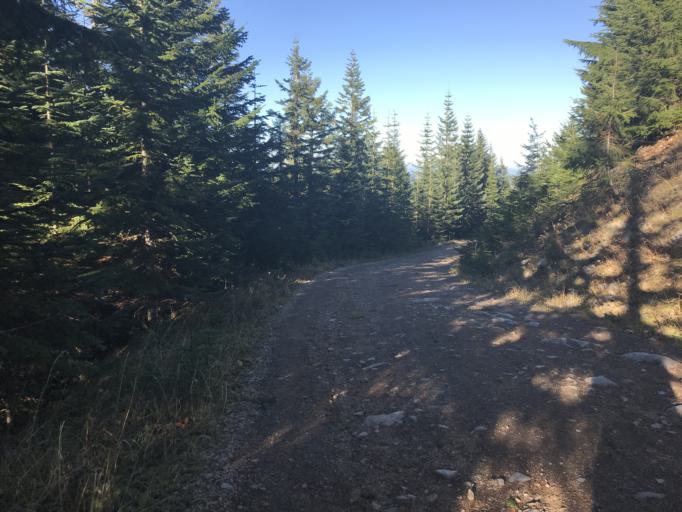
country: US
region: Washington
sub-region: King County
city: Enumclaw
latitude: 47.0420
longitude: -121.5969
